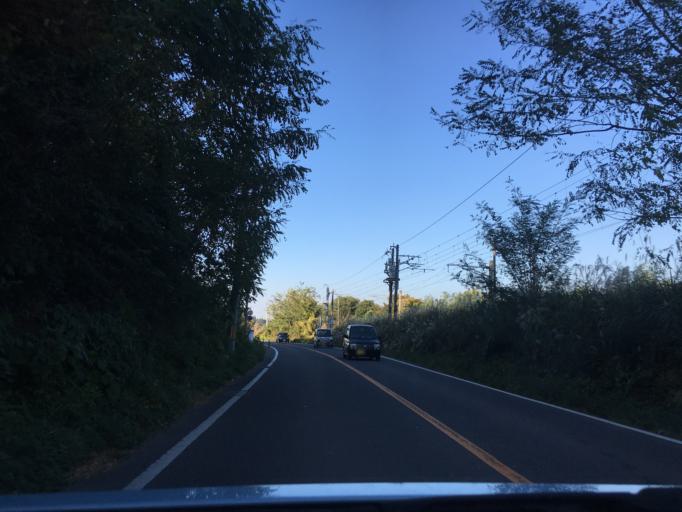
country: JP
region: Fukushima
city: Sukagawa
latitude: 37.3179
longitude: 140.3784
